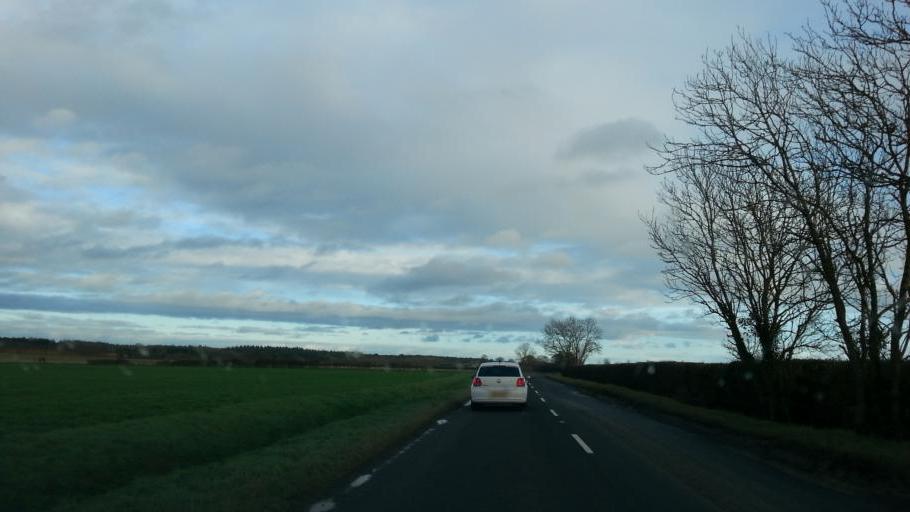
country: GB
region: England
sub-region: Oxfordshire
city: Stanford in the Vale
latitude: 51.6464
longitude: -1.5300
